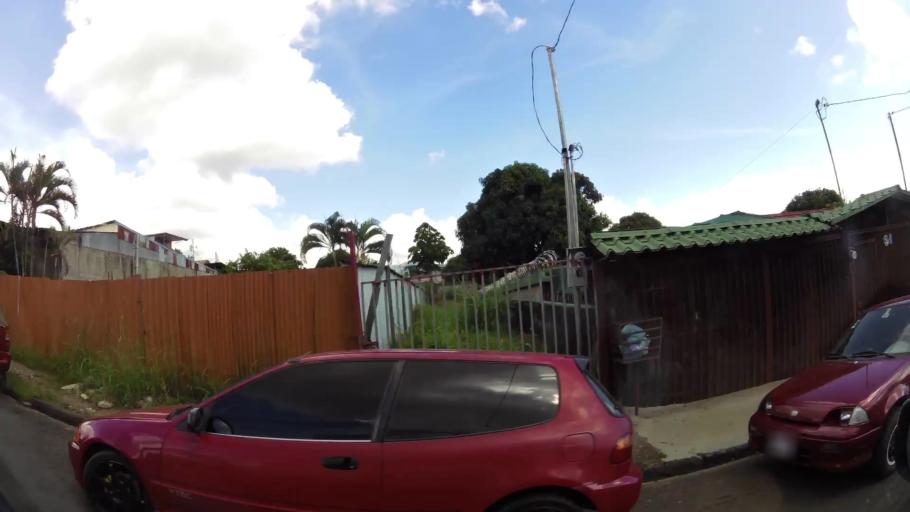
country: CR
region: San Jose
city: San Isidro
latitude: 9.3705
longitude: -83.7068
